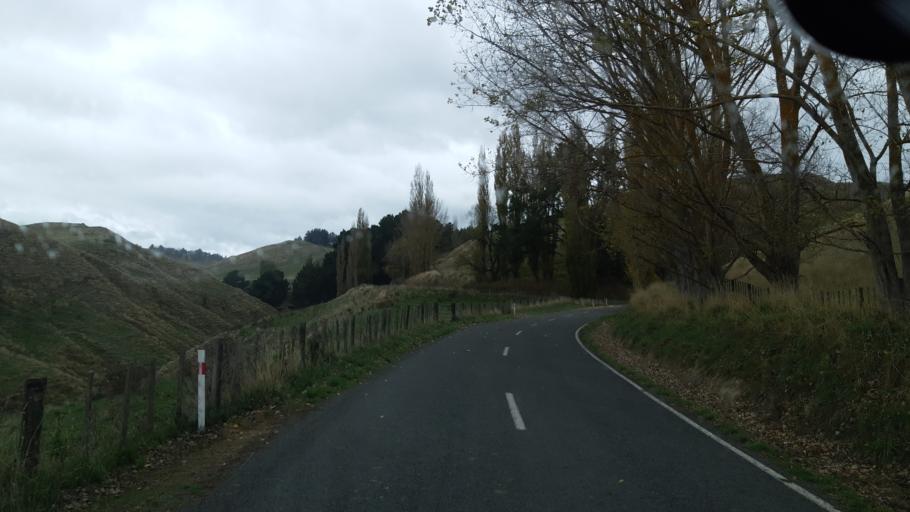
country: NZ
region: Manawatu-Wanganui
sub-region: Ruapehu District
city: Waiouru
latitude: -39.6117
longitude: 175.6133
